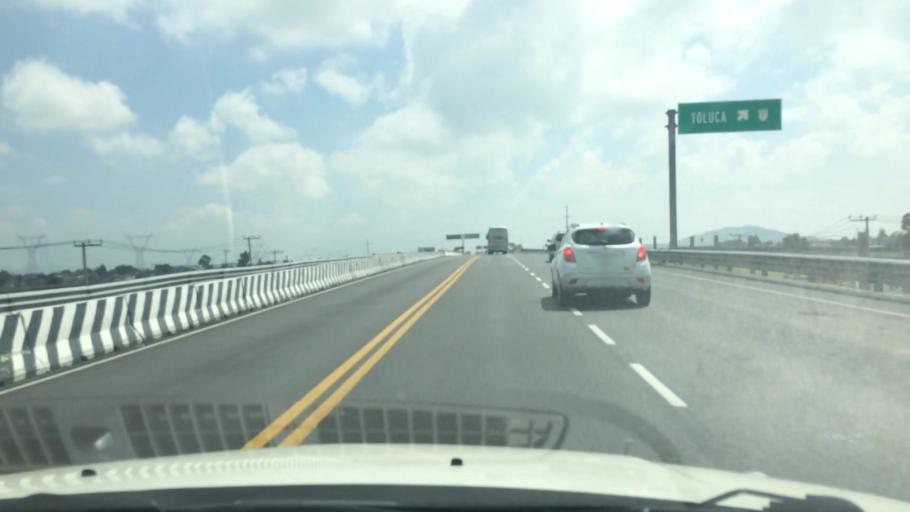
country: MX
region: Mexico
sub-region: Toluca
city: Sebastian Lerdo de Tejada
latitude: 19.3867
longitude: -99.7104
